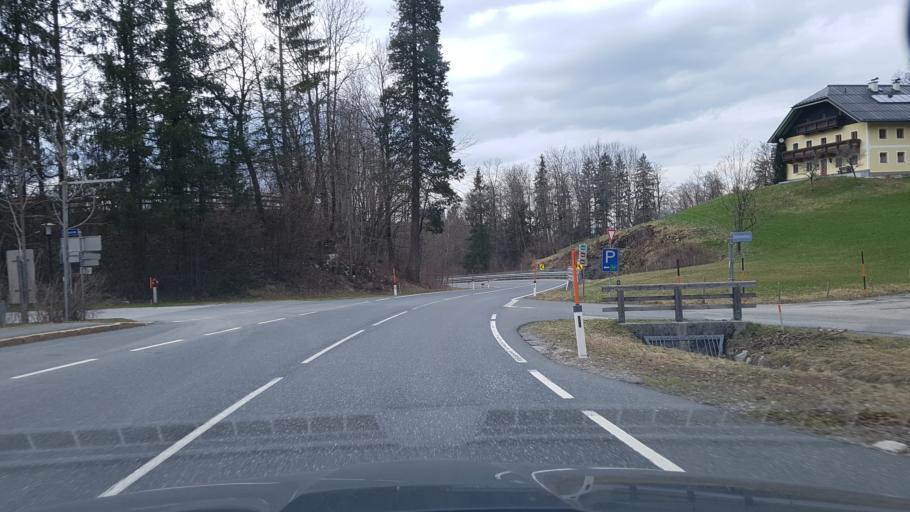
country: AT
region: Salzburg
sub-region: Politischer Bezirk Hallein
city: Hallein
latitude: 47.6670
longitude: 13.0930
